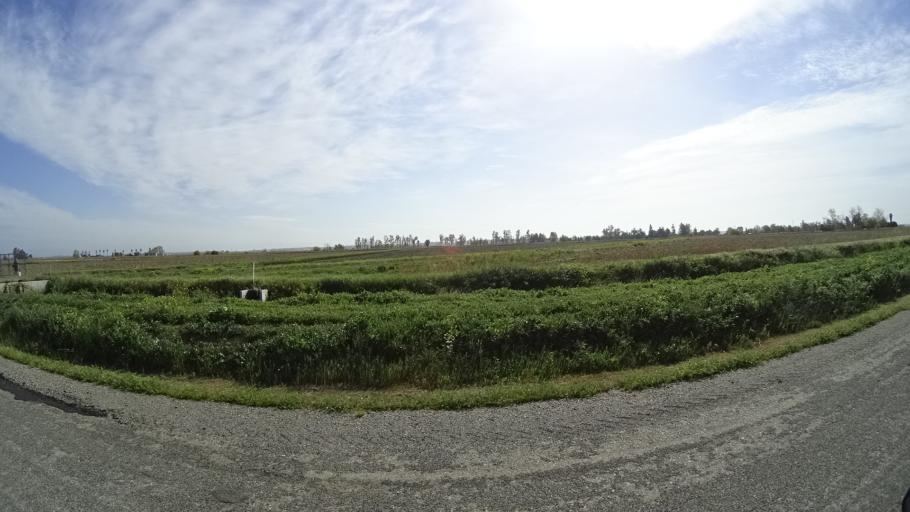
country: US
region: California
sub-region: Glenn County
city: Willows
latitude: 39.5854
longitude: -122.0466
